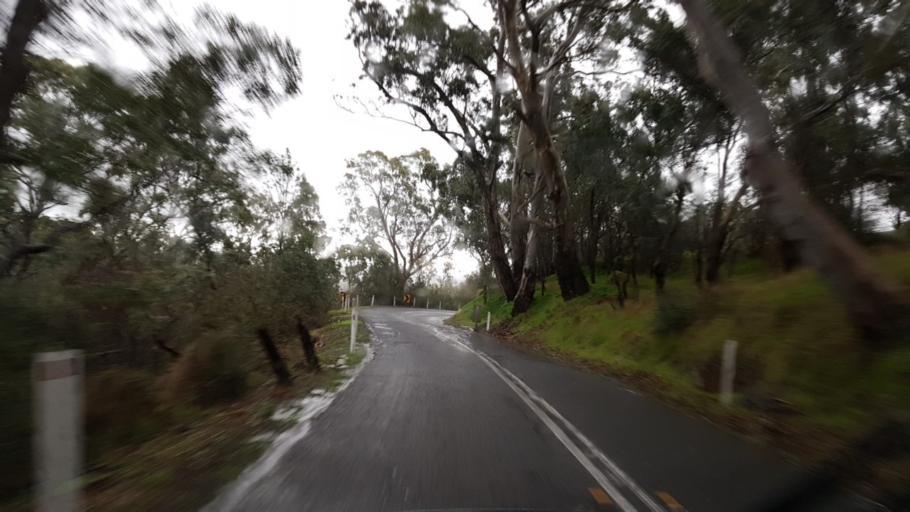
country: AU
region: South Australia
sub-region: Onkaparinga
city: Craigburn Farm
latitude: -35.0632
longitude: 138.6233
